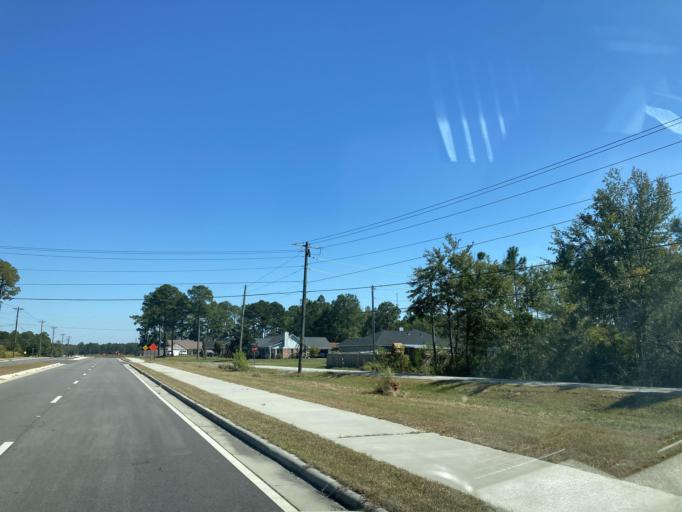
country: US
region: Mississippi
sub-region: Jackson County
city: Saint Martin
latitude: 30.4579
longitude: -88.8650
